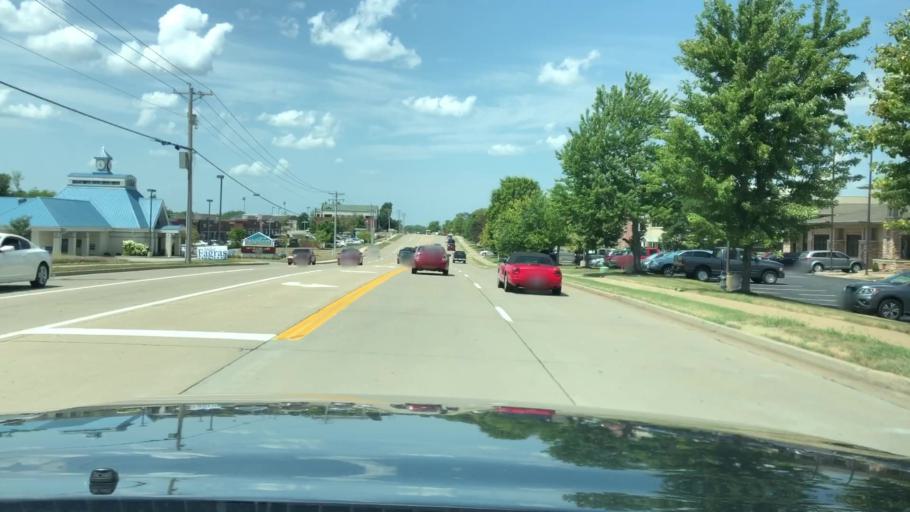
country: US
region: Missouri
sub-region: Saint Charles County
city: Saint Peters
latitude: 38.7923
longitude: -90.5847
